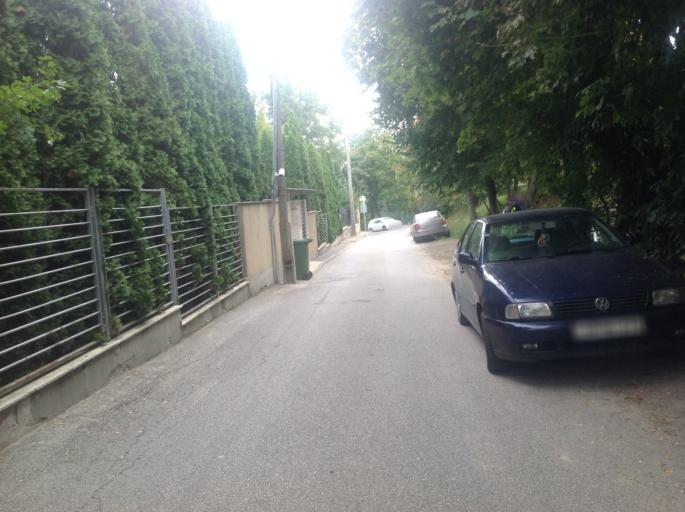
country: HU
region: Budapest
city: Budapest XII. keruelet
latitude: 47.4984
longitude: 18.9833
